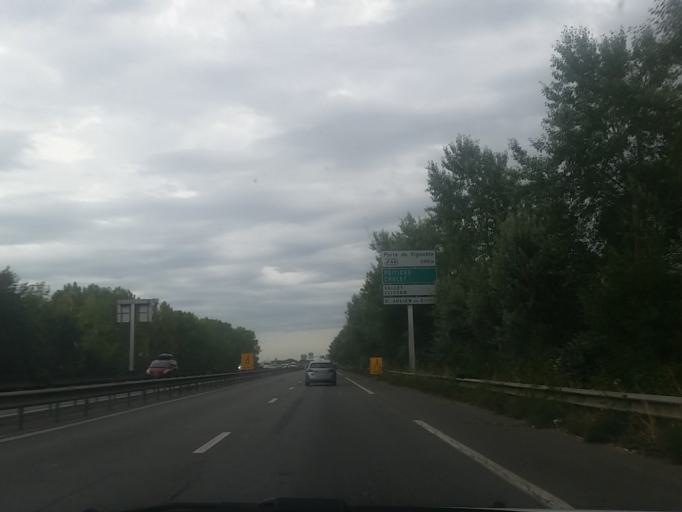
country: FR
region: Pays de la Loire
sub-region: Departement de la Loire-Atlantique
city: Basse-Goulaine
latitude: 47.2189
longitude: -1.4762
